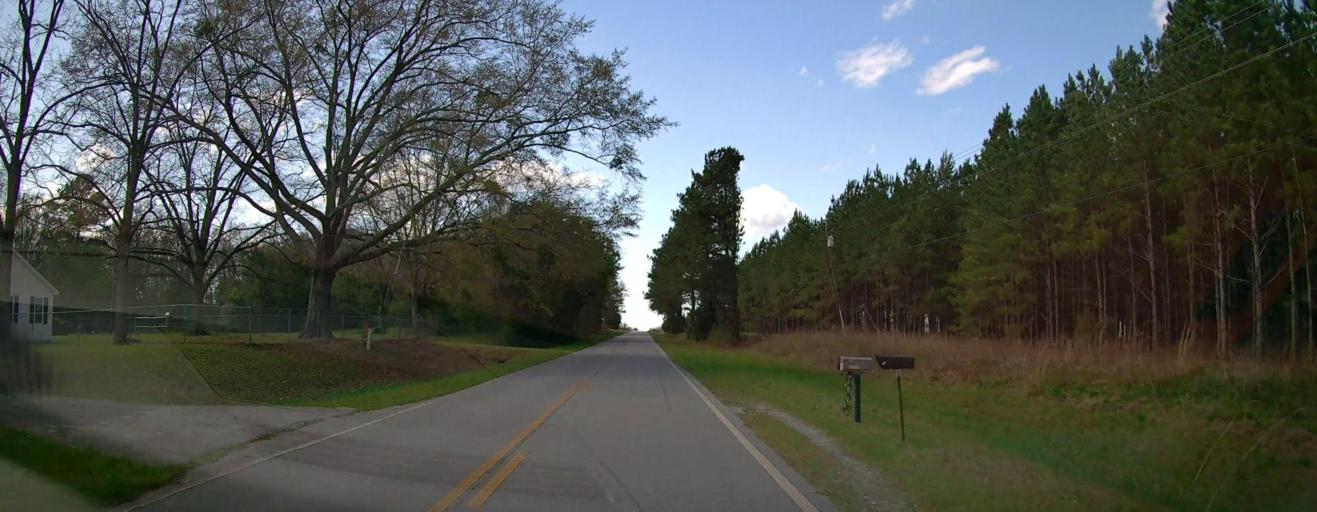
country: US
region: Georgia
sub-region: Wilkinson County
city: Gordon
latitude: 32.8280
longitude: -83.4258
